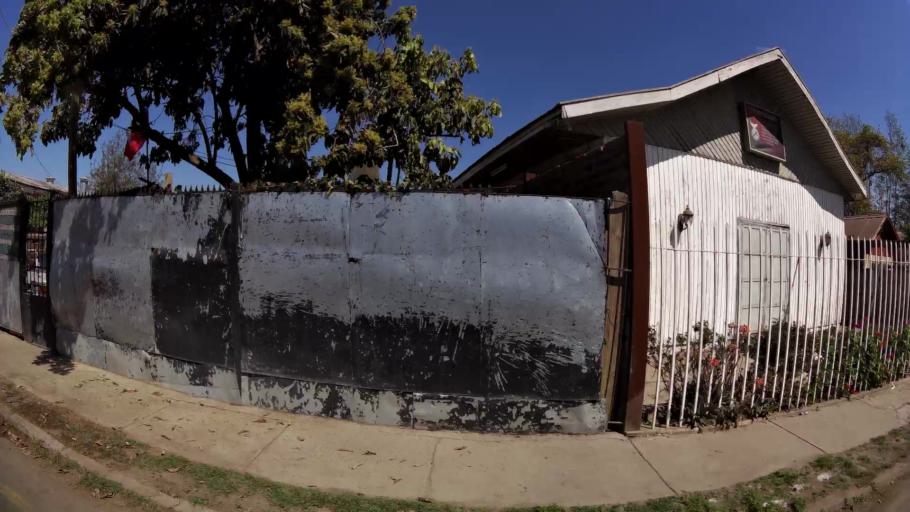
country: CL
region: Santiago Metropolitan
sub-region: Provincia de Santiago
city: Lo Prado
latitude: -33.4026
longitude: -70.7366
